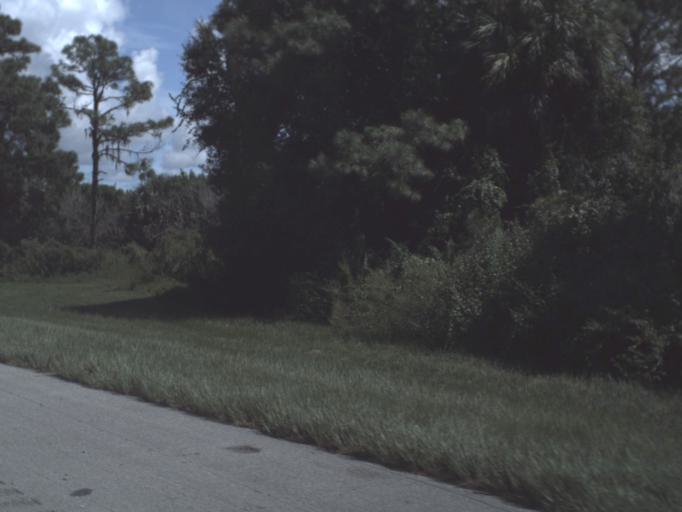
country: US
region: Florida
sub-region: Sarasota County
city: Vamo
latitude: 27.2331
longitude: -82.4520
